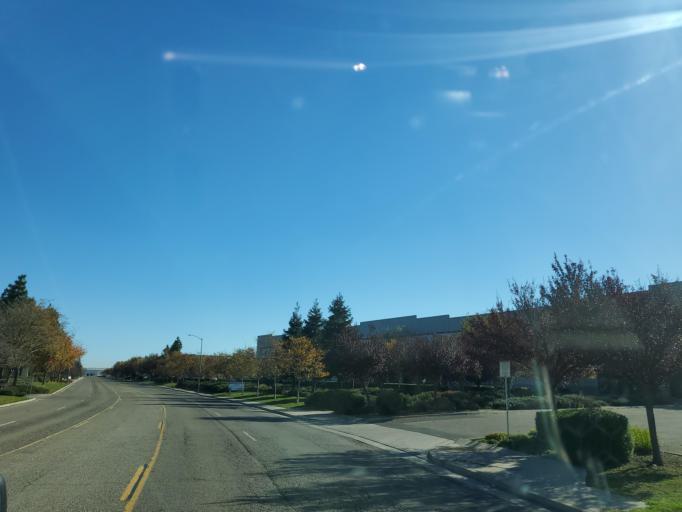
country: US
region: California
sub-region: San Joaquin County
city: Kennedy
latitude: 37.9113
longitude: -121.2533
